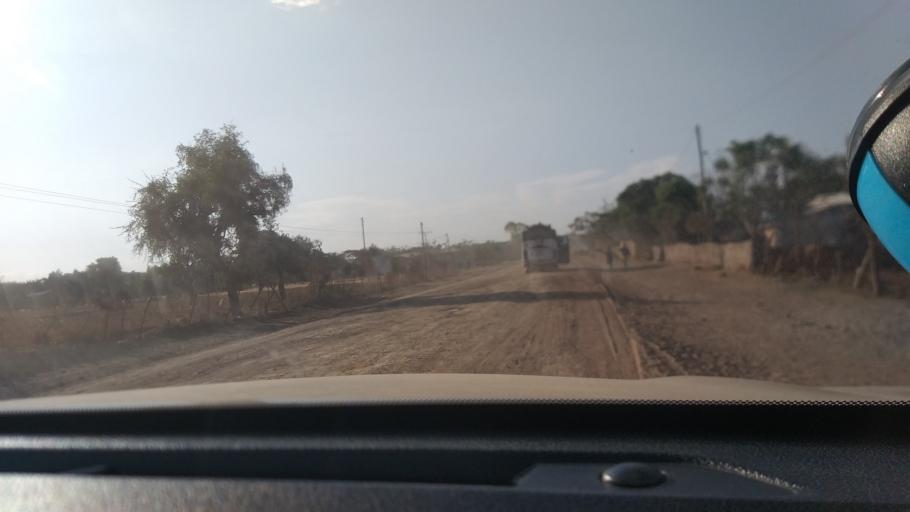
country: ET
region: Oromiya
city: Shashemene
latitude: 7.4888
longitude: 38.7217
